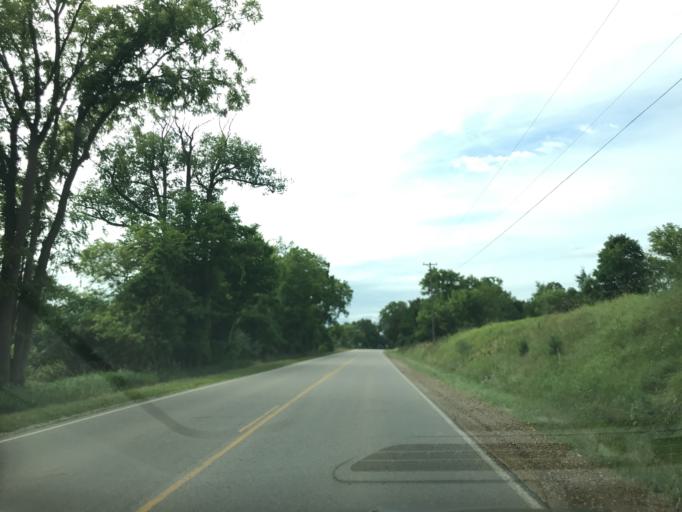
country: US
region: Michigan
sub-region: Jackson County
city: Spring Arbor
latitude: 42.0523
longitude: -84.5108
